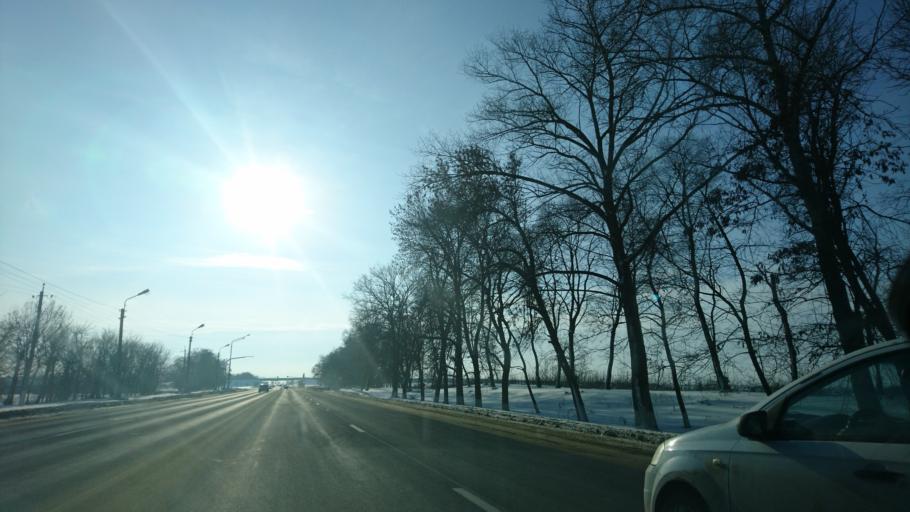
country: RU
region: Belgorod
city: Severnyy
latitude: 50.7294
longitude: 36.5295
